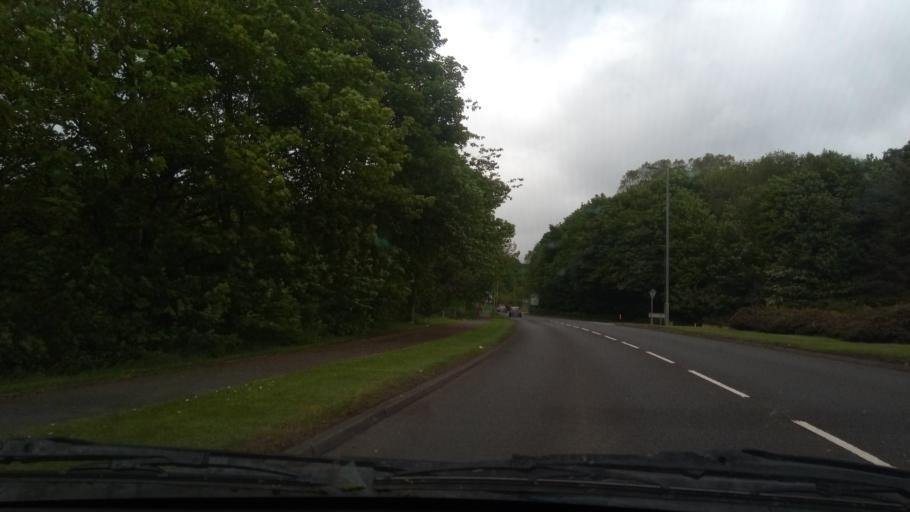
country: GB
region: Scotland
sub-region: The Scottish Borders
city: Hawick
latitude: 55.4336
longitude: -2.7800
